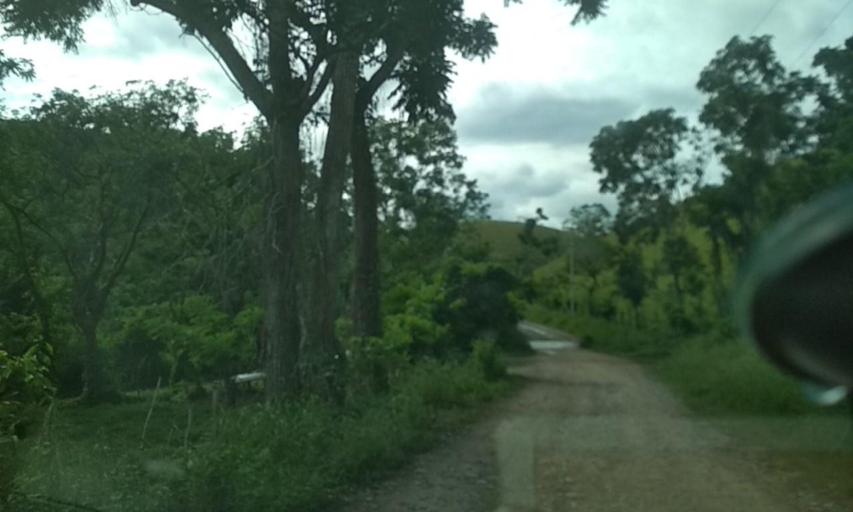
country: MX
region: Veracruz
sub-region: Papantla
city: Polutla
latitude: 20.5689
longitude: -97.1920
